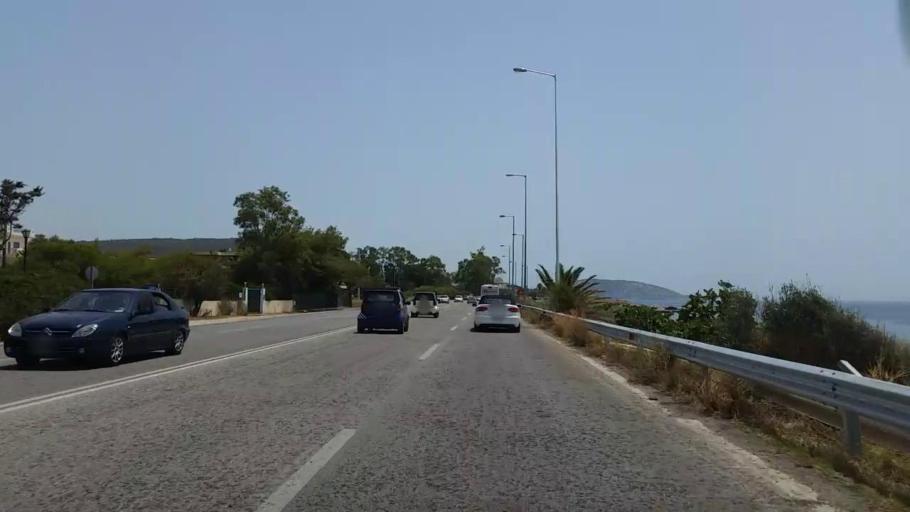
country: GR
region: Attica
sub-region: Nomarchia Anatolikis Attikis
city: Saronida
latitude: 37.7577
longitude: 23.9024
